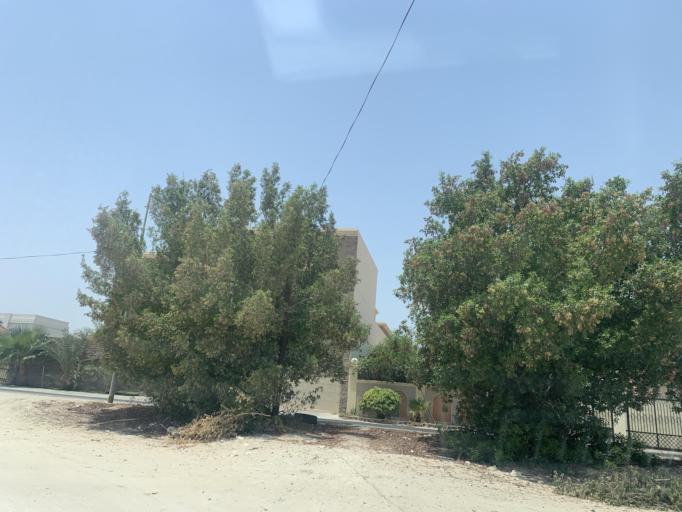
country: BH
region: Manama
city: Jidd Hafs
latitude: 26.2076
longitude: 50.4707
